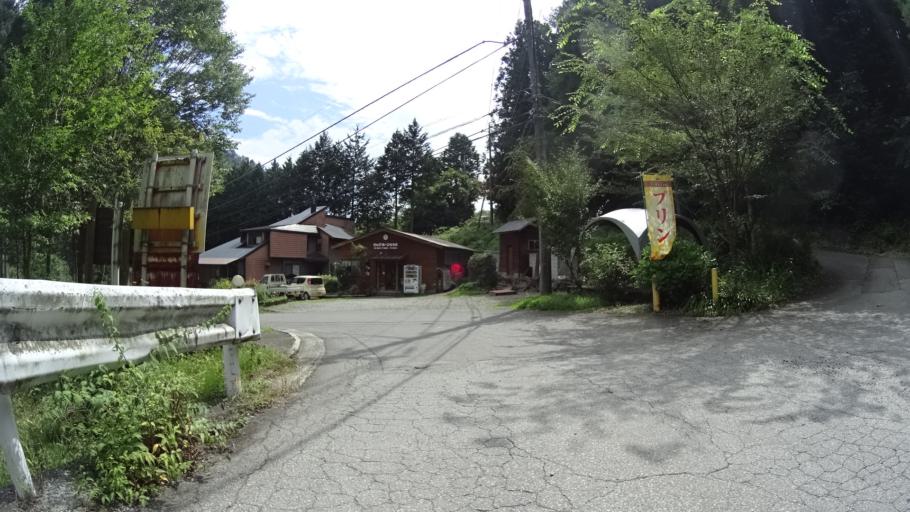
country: JP
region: Yamanashi
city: Nirasaki
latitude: 35.7788
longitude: 138.5352
